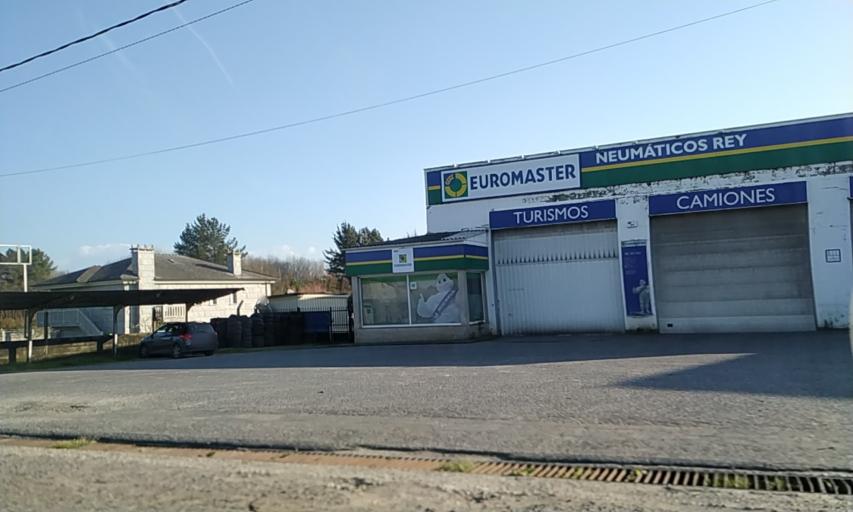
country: ES
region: Galicia
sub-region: Provincia de Lugo
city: Corgo
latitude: 42.9486
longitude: -7.4487
